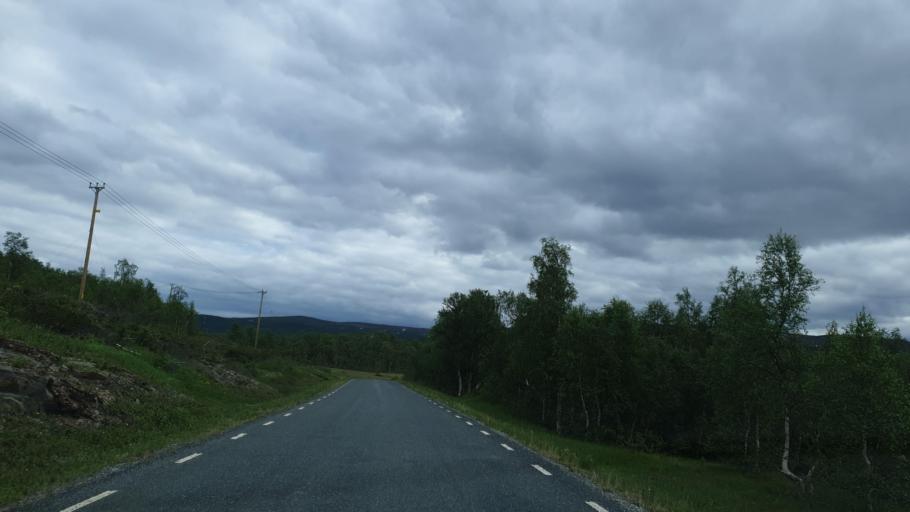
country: NO
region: Nordland
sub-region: Hattfjelldal
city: Hattfjelldal
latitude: 65.4198
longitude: 14.6771
